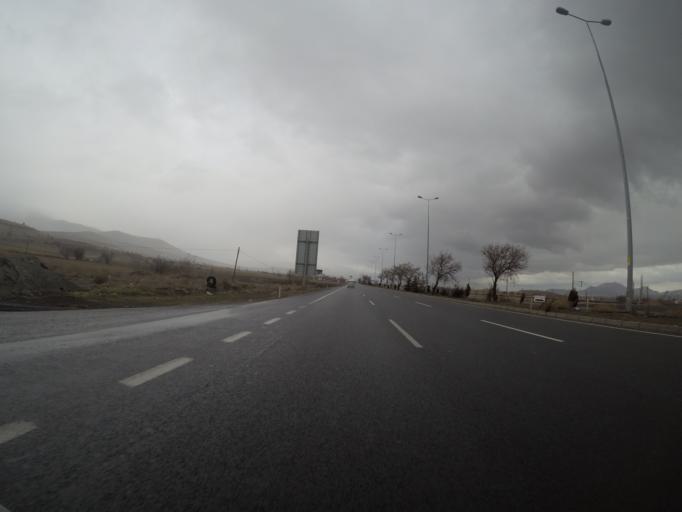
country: TR
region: Kayseri
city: Incesu
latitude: 38.6867
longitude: 35.2393
